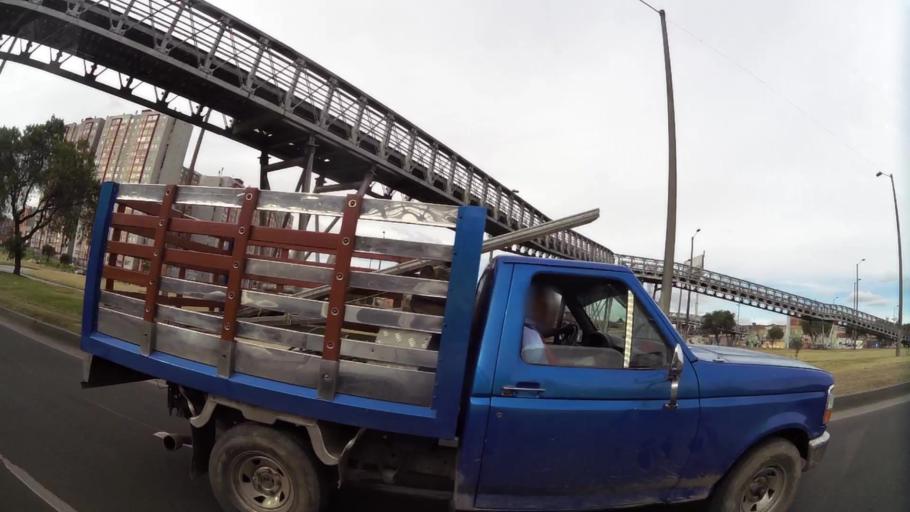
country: CO
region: Bogota D.C.
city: Bogota
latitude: 4.6349
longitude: -74.1531
